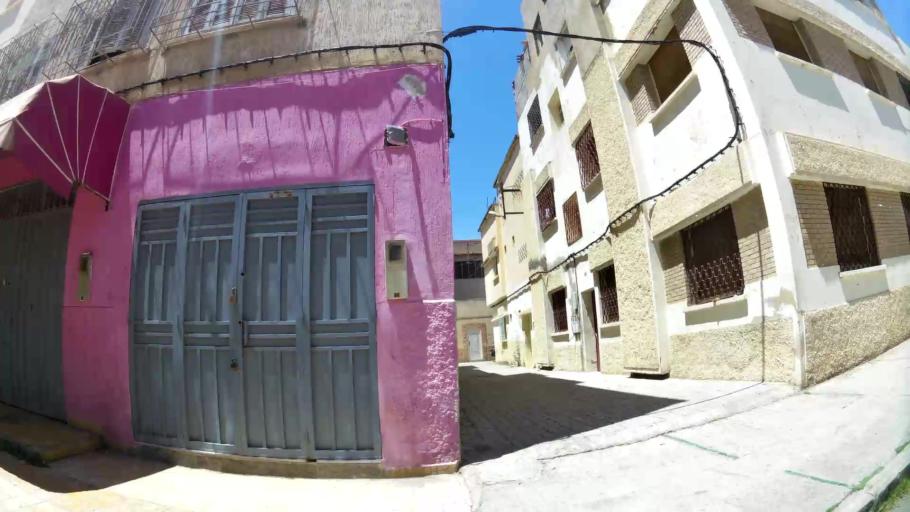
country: MA
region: Fes-Boulemane
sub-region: Fes
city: Fes
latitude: 34.0234
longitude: -5.0070
